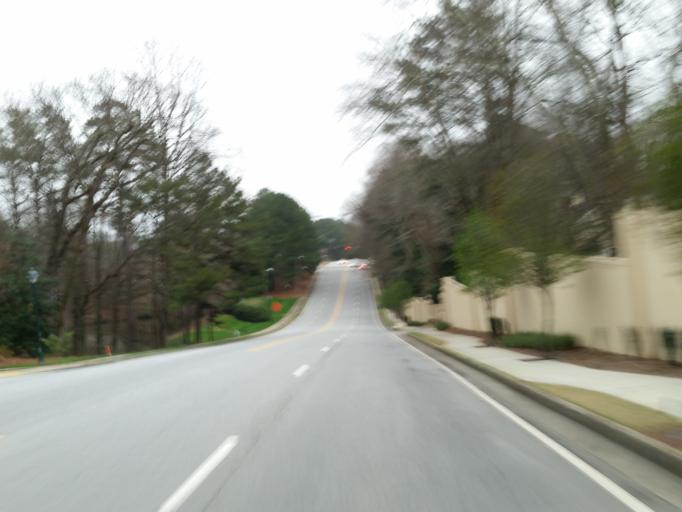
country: US
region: Georgia
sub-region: Fulton County
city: Sandy Springs
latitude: 33.9193
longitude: -84.3897
